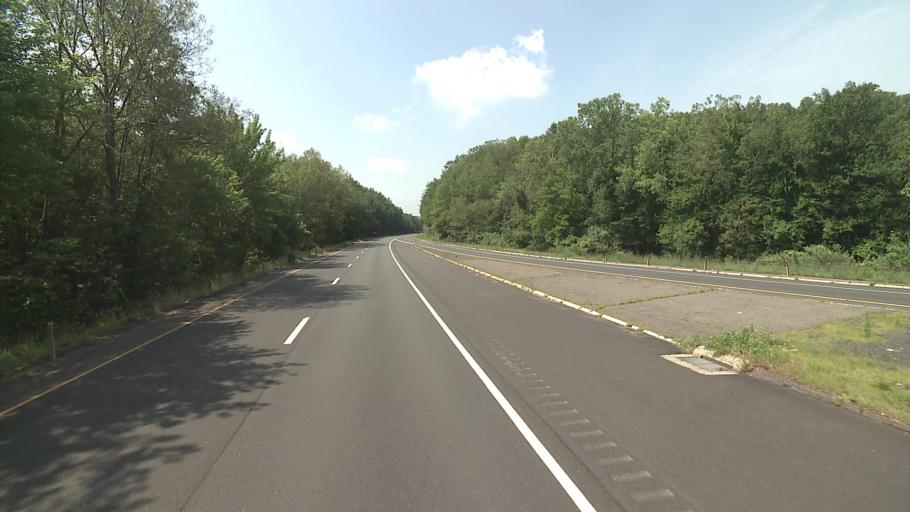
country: US
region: Connecticut
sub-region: Hartford County
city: Manchester
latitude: 41.7771
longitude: -72.4641
